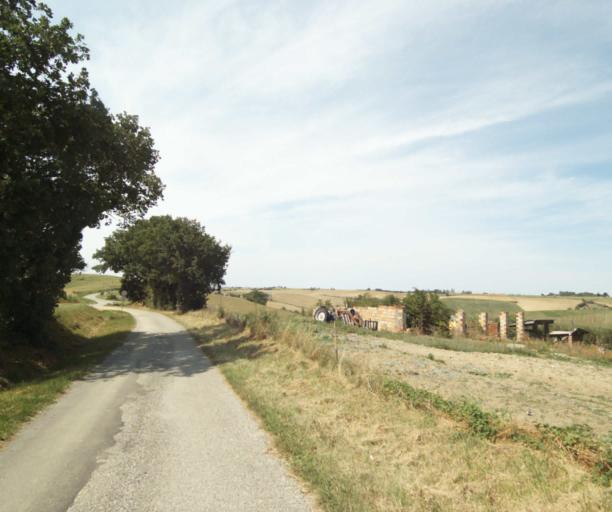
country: FR
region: Midi-Pyrenees
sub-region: Departement de l'Ariege
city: Lezat-sur-Leze
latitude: 43.2527
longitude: 1.4054
